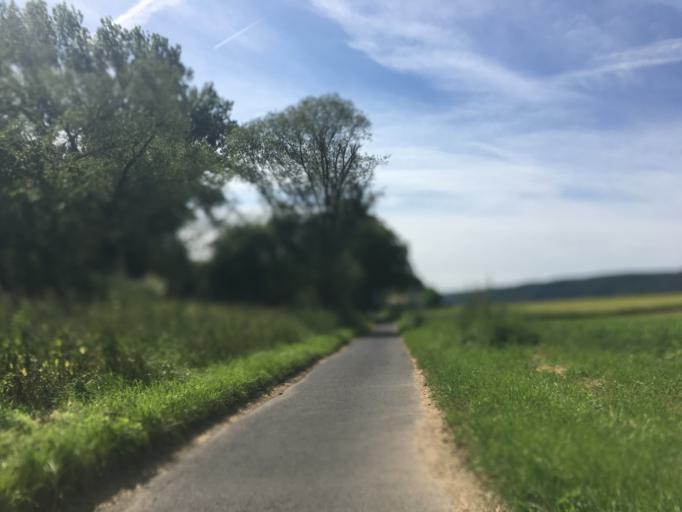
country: DE
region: Rheinland-Pfalz
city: Dattenberg
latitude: 50.5495
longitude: 7.2786
